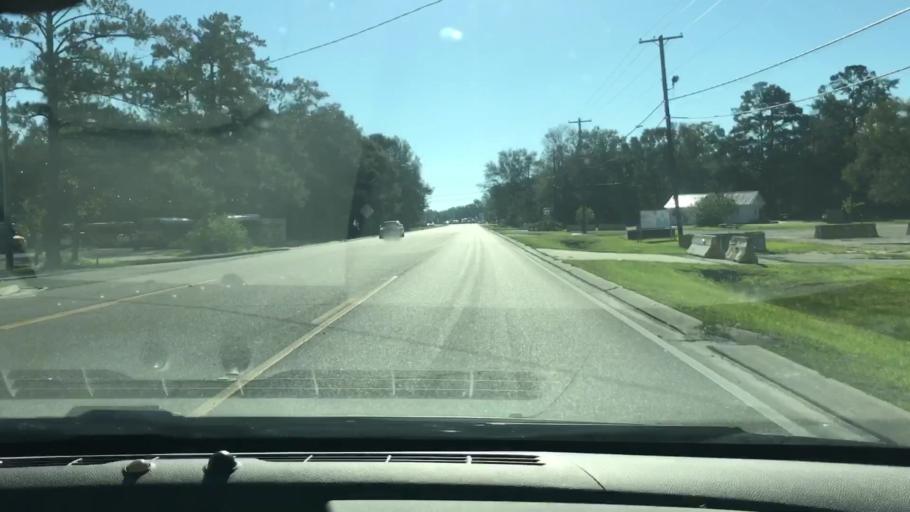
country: US
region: Louisiana
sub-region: Saint Tammany Parish
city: Pearl River
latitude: 30.3664
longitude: -89.7585
